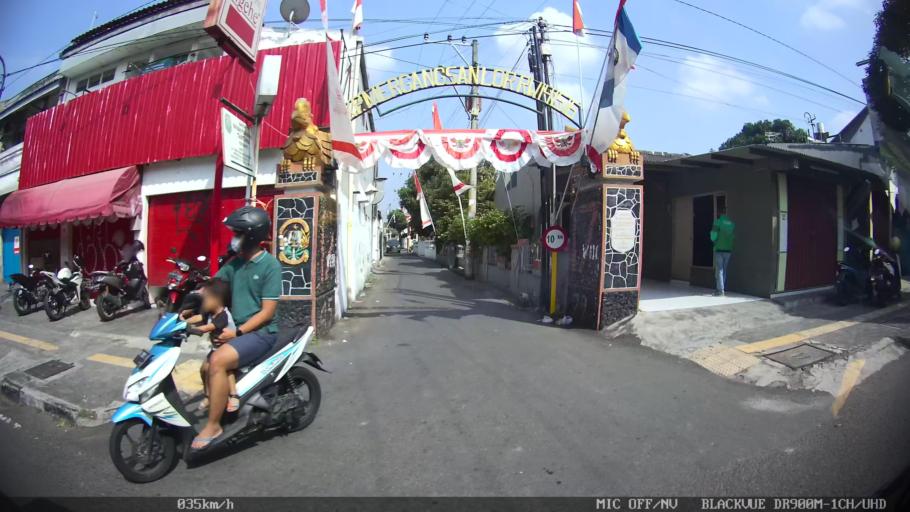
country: ID
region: Daerah Istimewa Yogyakarta
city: Yogyakarta
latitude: -7.8084
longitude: 110.3773
